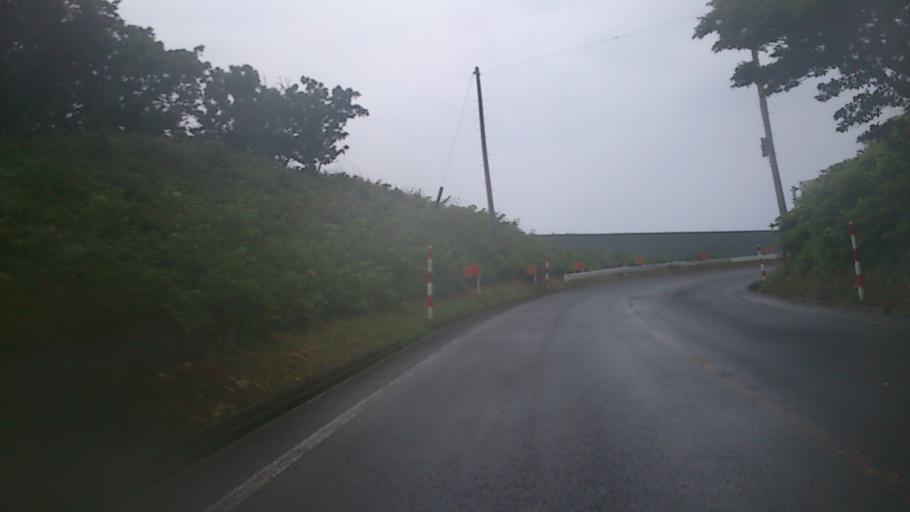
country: JP
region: Akita
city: Noshiromachi
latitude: 40.4283
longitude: 139.9411
